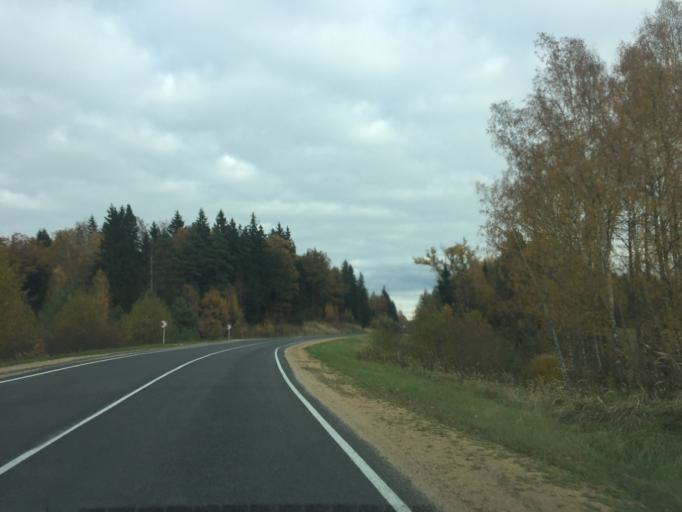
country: BY
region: Minsk
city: Svir
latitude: 54.8657
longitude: 26.3401
